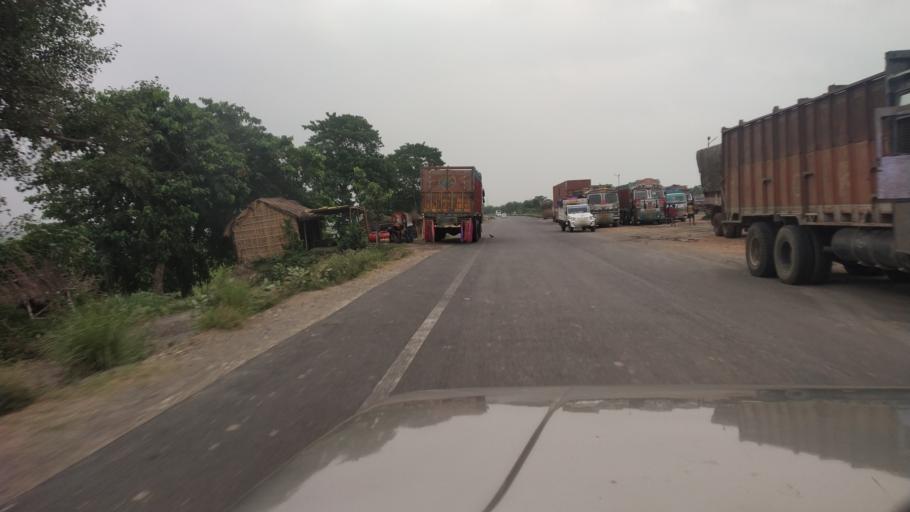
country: IN
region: Bihar
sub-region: Bhagalpur
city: Bhagalpur
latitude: 25.4018
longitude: 86.8073
